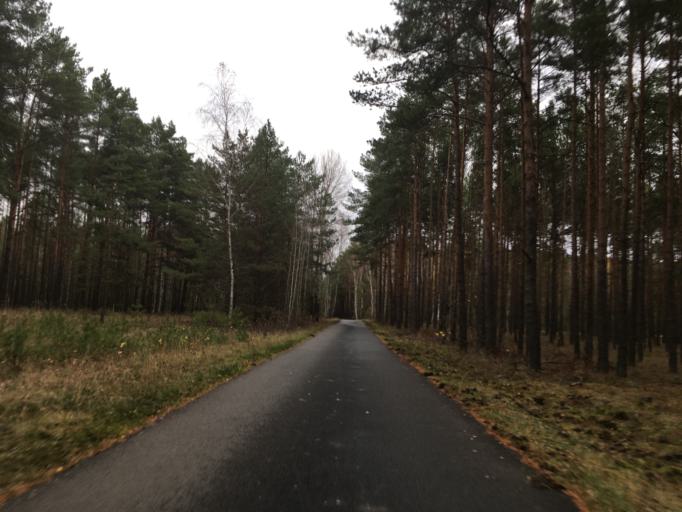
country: DE
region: Brandenburg
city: Mullrose
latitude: 52.2298
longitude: 14.4463
